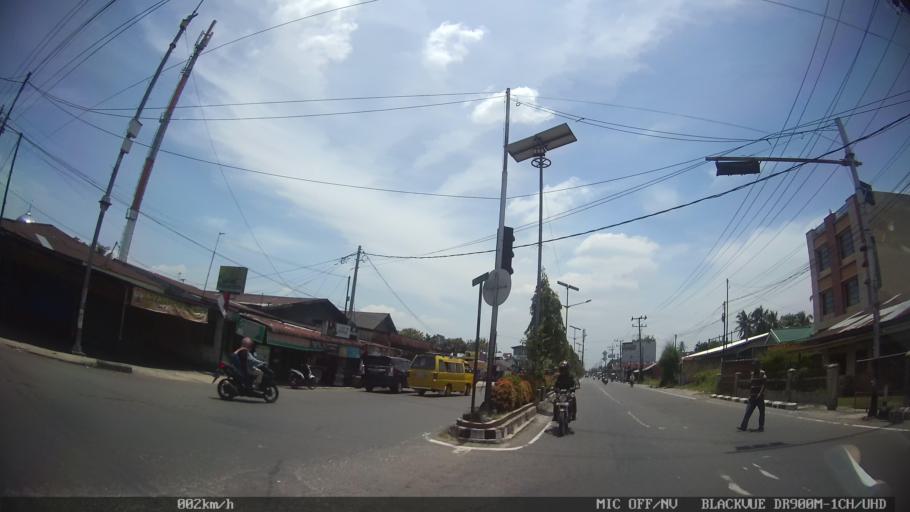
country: ID
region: North Sumatra
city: Binjai
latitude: 3.6080
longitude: 98.5180
